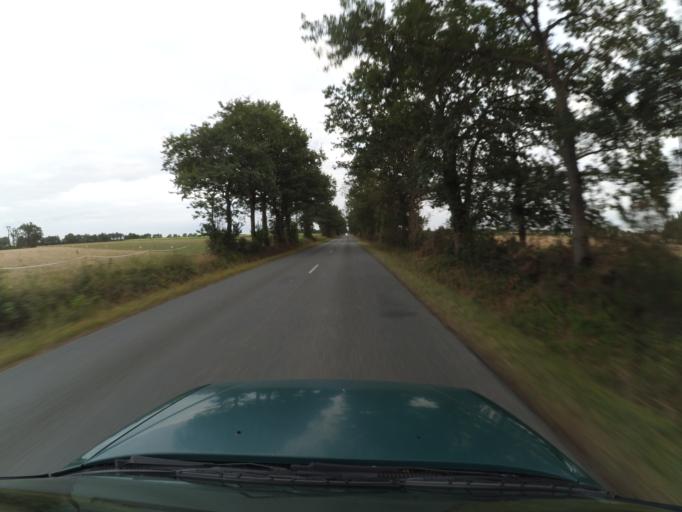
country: FR
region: Pays de la Loire
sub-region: Departement de la Loire-Atlantique
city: La Planche
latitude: 47.0096
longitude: -1.4772
